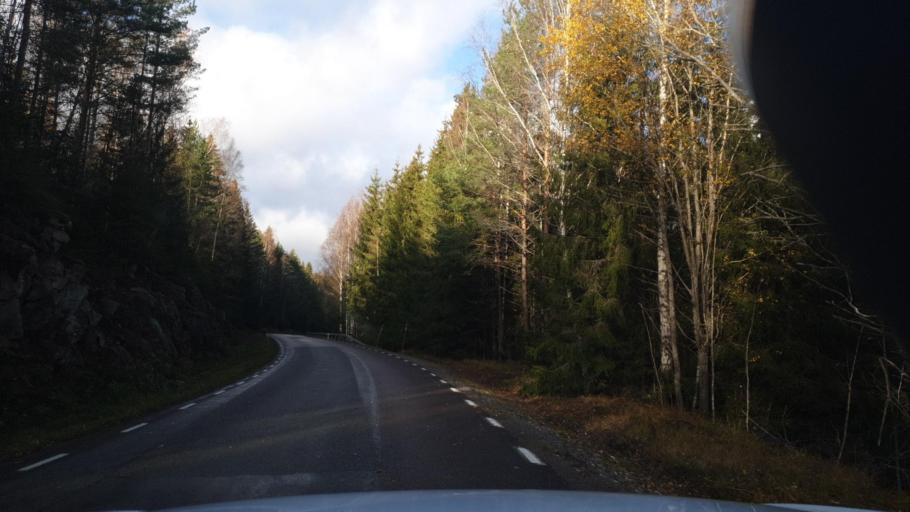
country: SE
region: Vaermland
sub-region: Grums Kommun
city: Grums
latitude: 59.5094
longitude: 12.8682
